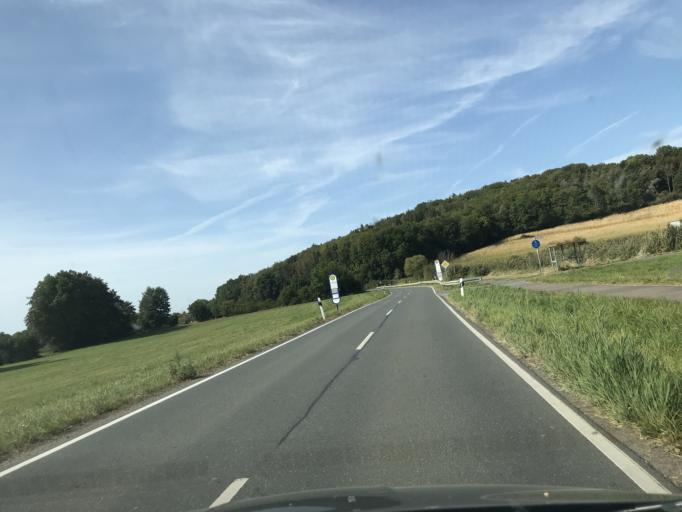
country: DE
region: Hesse
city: Gross-Umstadt
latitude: 49.8434
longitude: 8.9444
